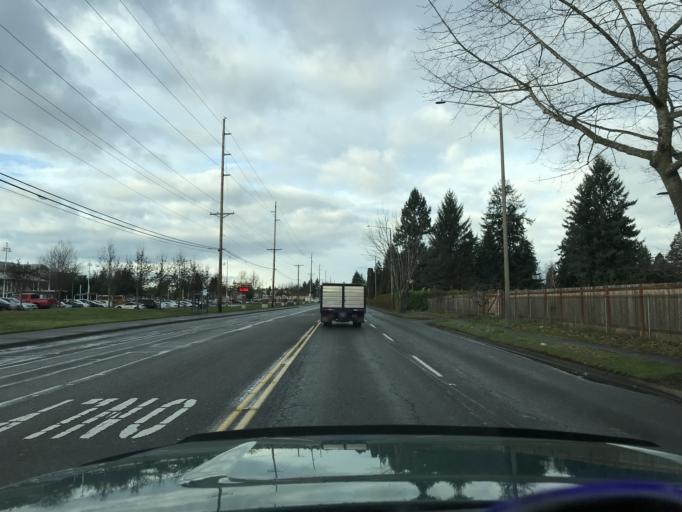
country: US
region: Washington
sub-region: Pierce County
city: Lakewood
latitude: 47.1906
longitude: -122.5004
